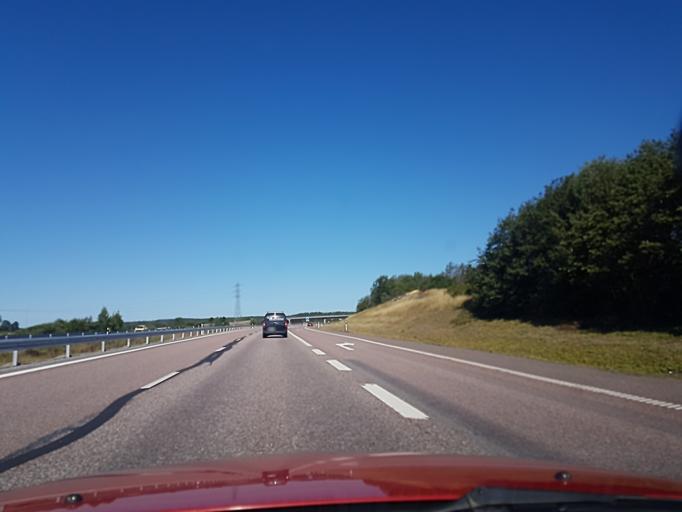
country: SE
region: Soedermanland
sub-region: Strangnas Kommun
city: Akers Styckebruk
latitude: 59.2768
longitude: 17.1176
